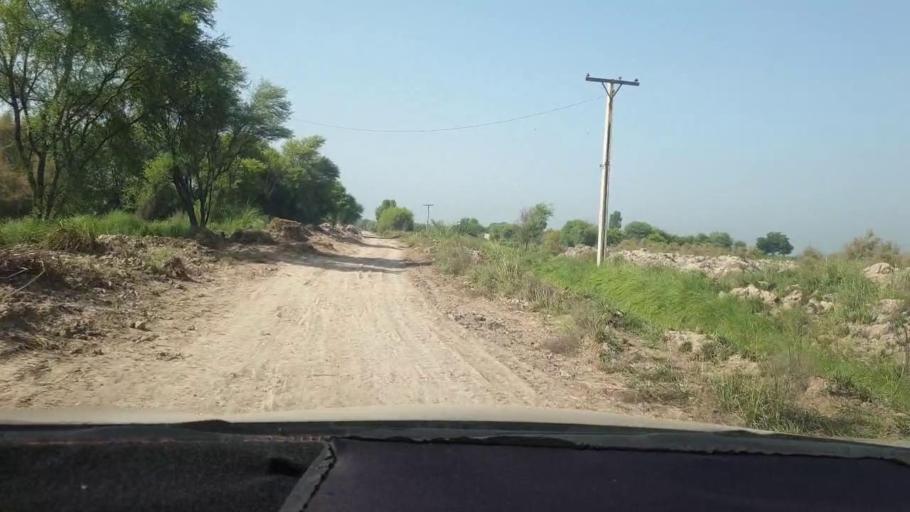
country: PK
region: Sindh
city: Miro Khan
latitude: 27.7208
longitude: 68.1133
